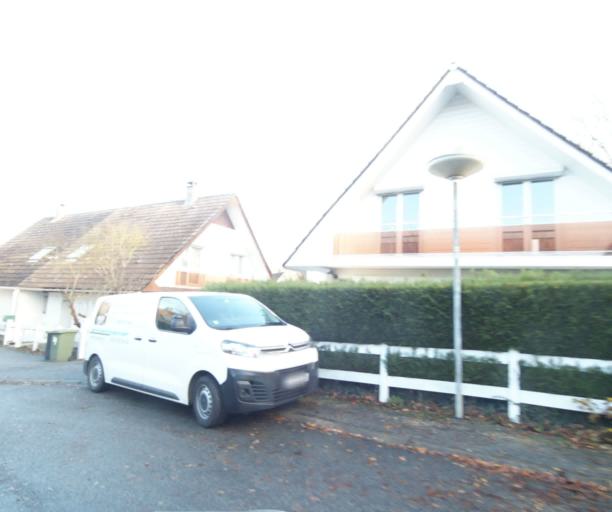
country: FR
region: Ile-de-France
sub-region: Departement des Yvelines
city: Meulan-en-Yvelines
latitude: 49.0109
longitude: 1.9254
